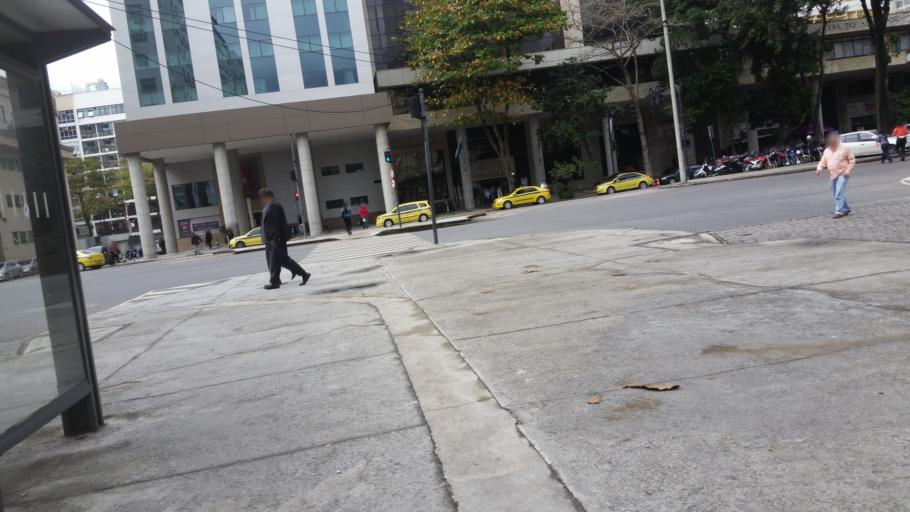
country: BR
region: Rio de Janeiro
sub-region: Rio De Janeiro
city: Rio de Janeiro
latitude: -22.9088
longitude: -43.1700
